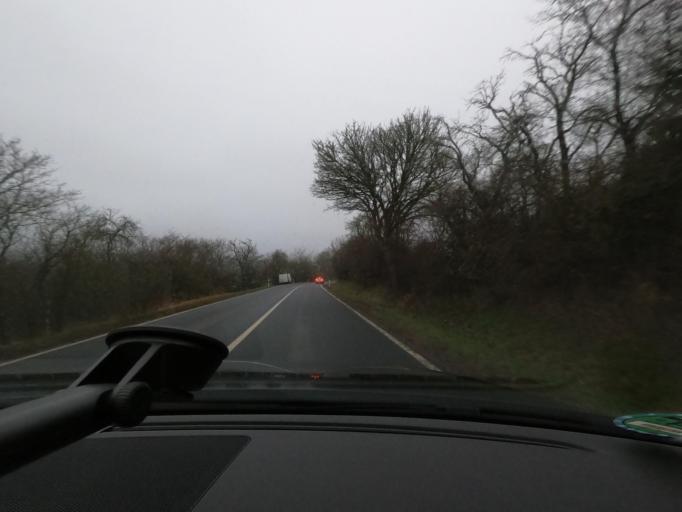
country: DE
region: Thuringia
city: Behringen
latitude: 50.7735
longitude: 11.0006
